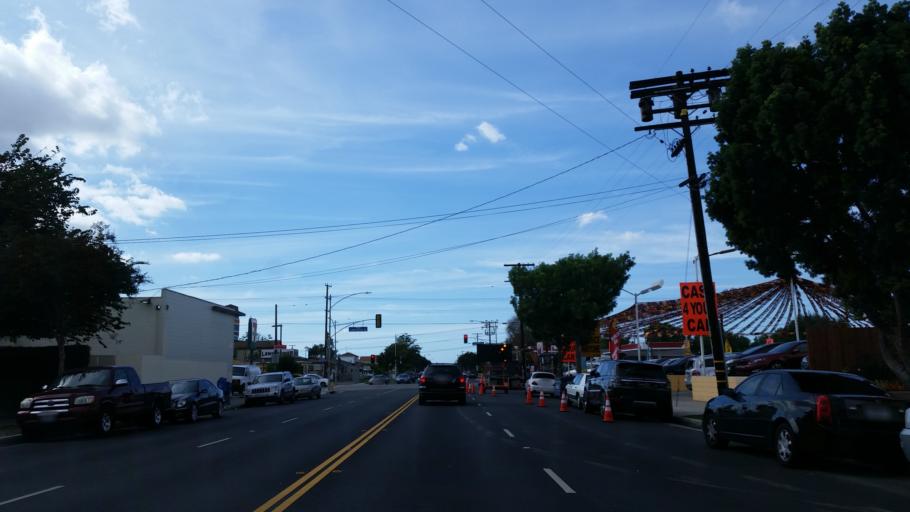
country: US
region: California
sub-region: Los Angeles County
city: Paramount
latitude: 33.8821
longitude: -118.1416
